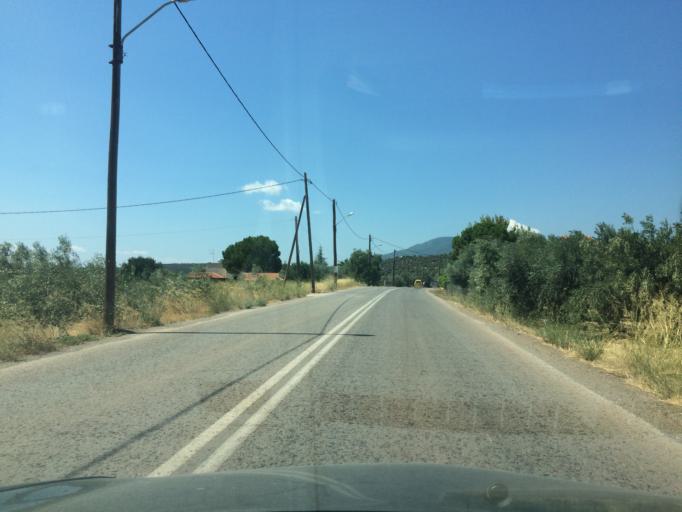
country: GR
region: Central Greece
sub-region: Nomos Evvoias
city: Psachna
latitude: 38.5792
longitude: 23.6261
